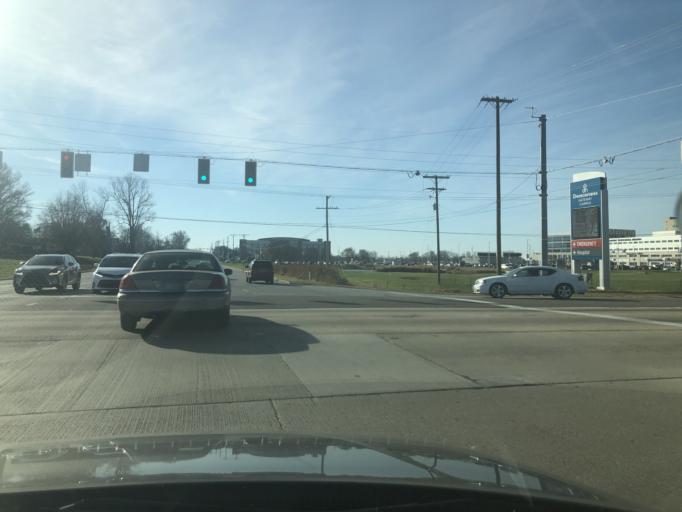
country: US
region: Indiana
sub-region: Warrick County
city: Newburgh
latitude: 37.9768
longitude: -87.4412
